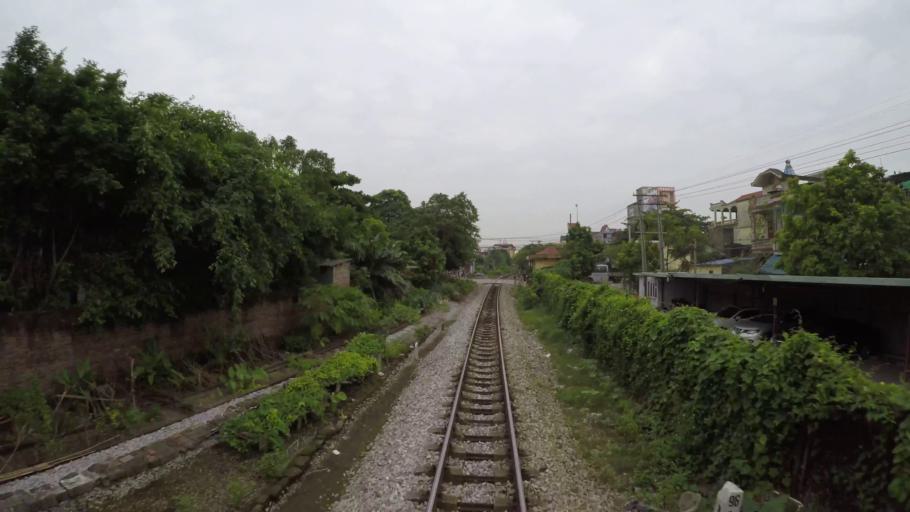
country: VN
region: Hai Phong
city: An Duong
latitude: 20.8864
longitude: 106.6005
